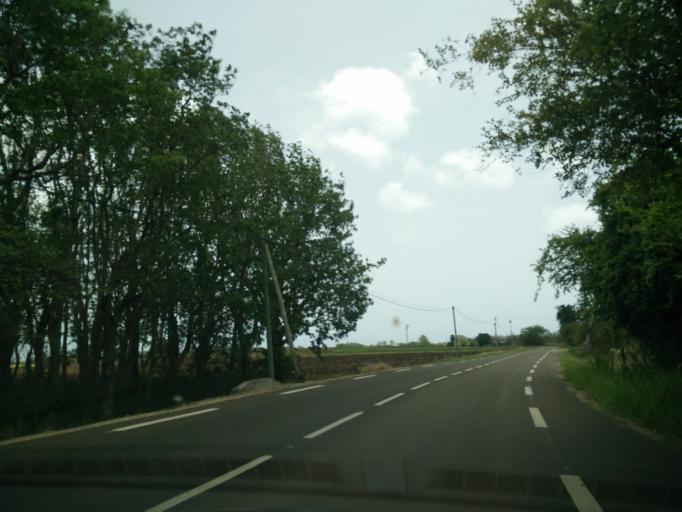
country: GP
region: Guadeloupe
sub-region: Guadeloupe
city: Anse-Bertrand
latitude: 16.4610
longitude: -61.5113
